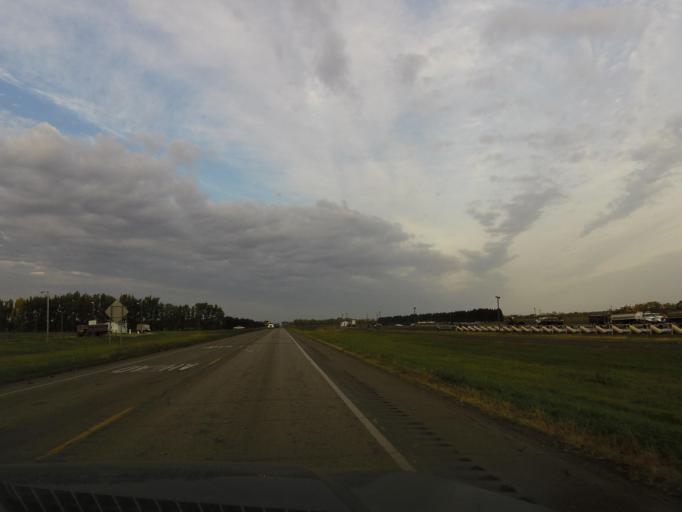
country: US
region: North Dakota
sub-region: Walsh County
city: Grafton
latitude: 48.6010
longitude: -97.4539
